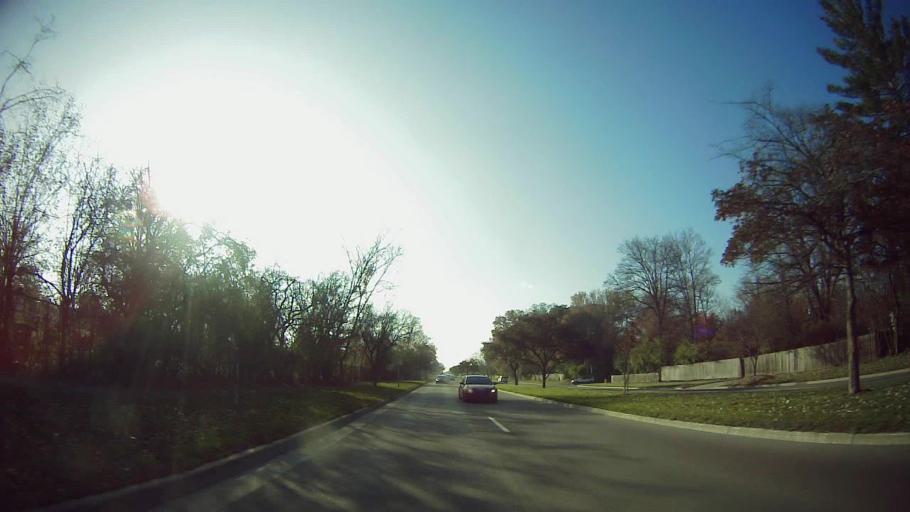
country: US
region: Michigan
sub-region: Oakland County
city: Berkley
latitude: 42.5063
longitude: -83.1839
